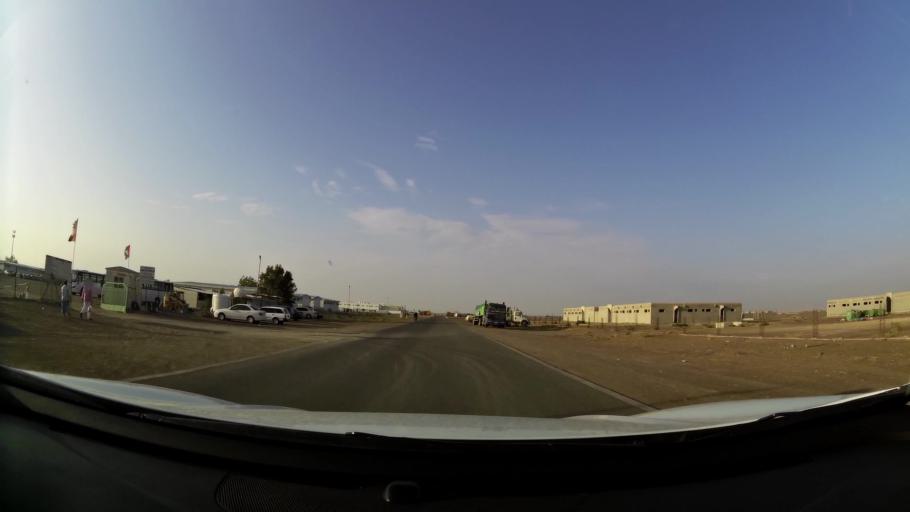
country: AE
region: Abu Dhabi
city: Al Ain
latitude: 24.1436
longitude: 55.8455
